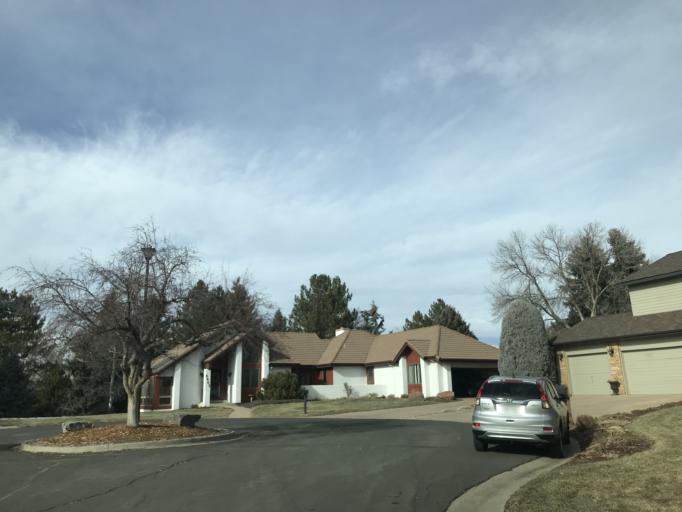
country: US
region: Colorado
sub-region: Arapahoe County
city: Littleton
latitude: 39.5961
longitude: -105.0105
